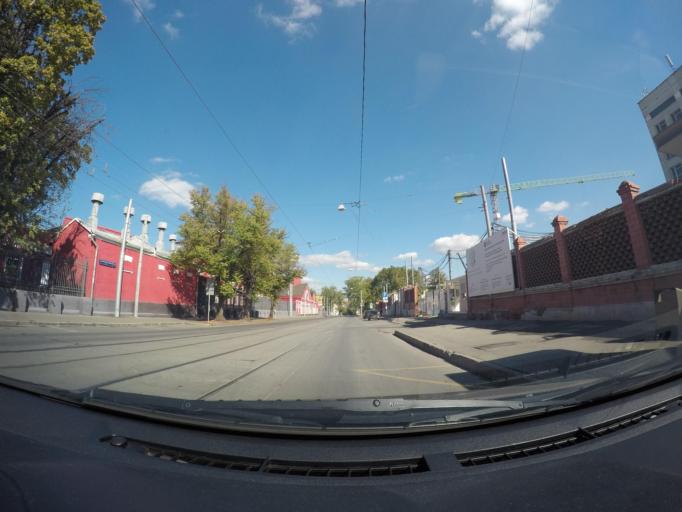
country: RU
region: Moscow
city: Lefortovo
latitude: 55.7887
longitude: 37.6927
